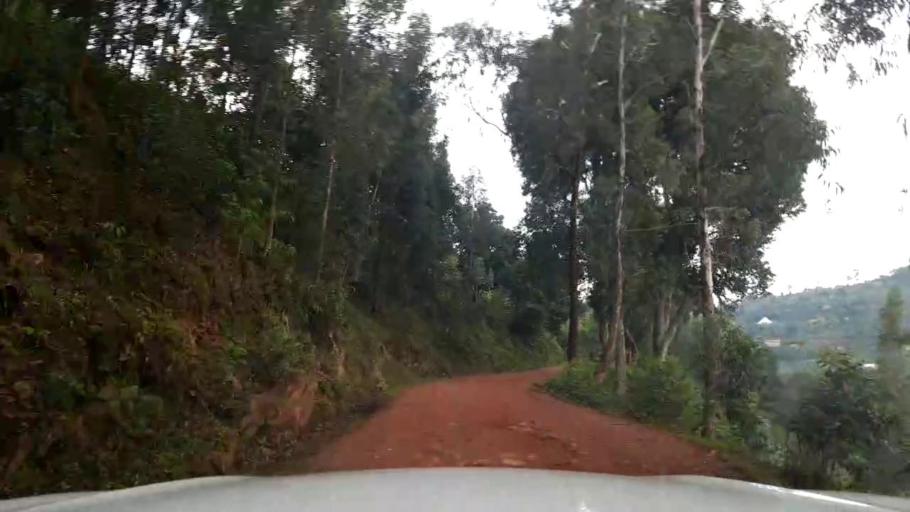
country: UG
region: Western Region
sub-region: Kisoro District
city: Kisoro
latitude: -1.4000
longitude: 29.8014
